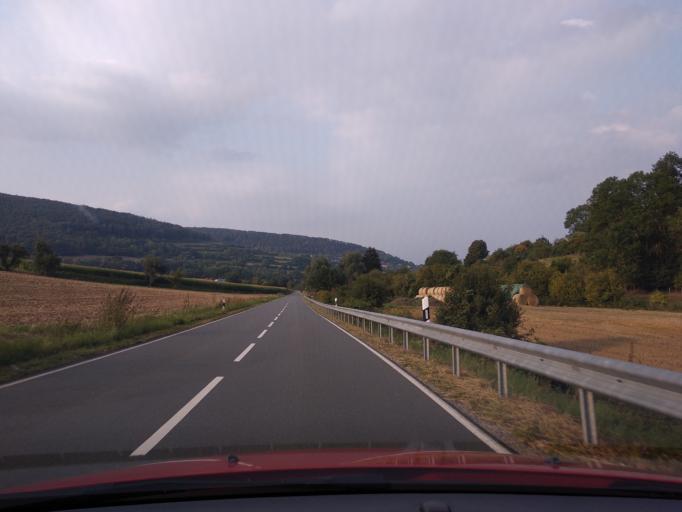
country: DE
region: North Rhine-Westphalia
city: Beverungen
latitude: 51.6512
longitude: 9.3507
